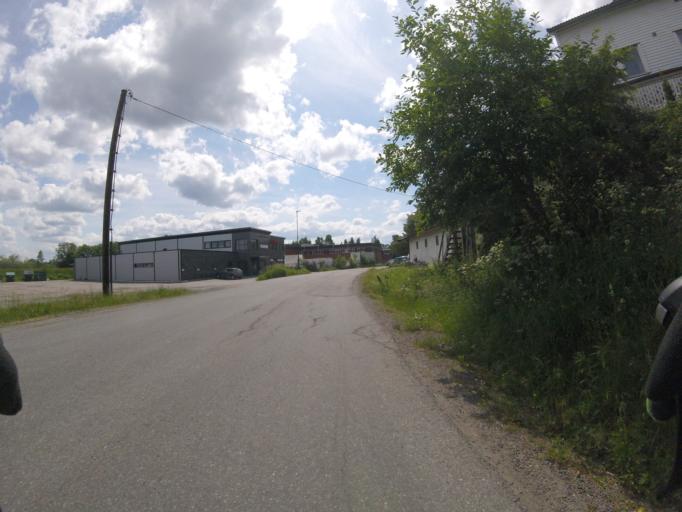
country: NO
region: Akershus
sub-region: Skedsmo
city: Lillestrom
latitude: 59.9593
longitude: 11.0214
